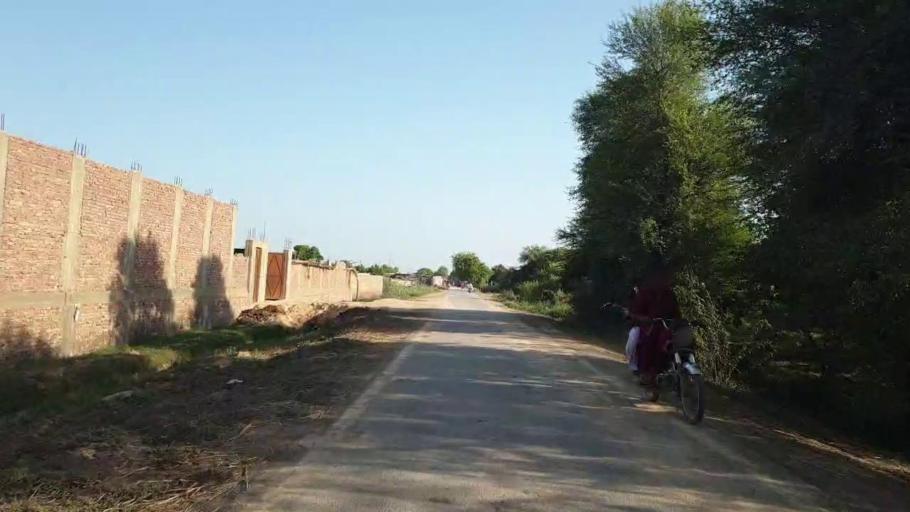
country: PK
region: Sindh
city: Hyderabad
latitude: 25.3445
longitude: 68.4164
